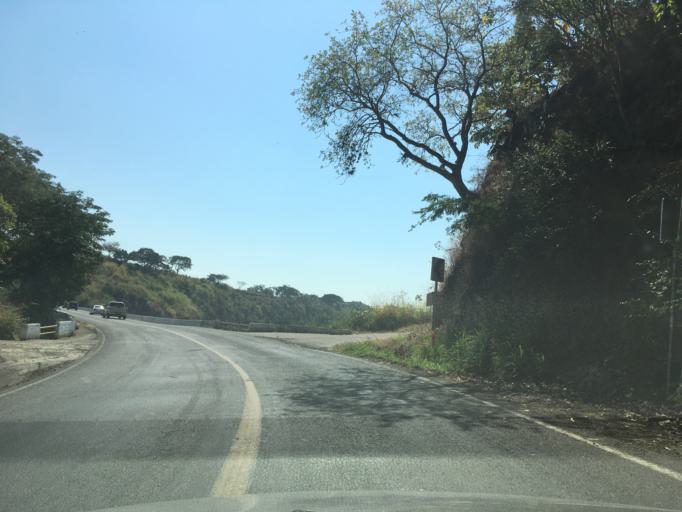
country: MX
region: Michoacan
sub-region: Gabriel Zamora
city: Lombardia
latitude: 19.2259
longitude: -102.0500
